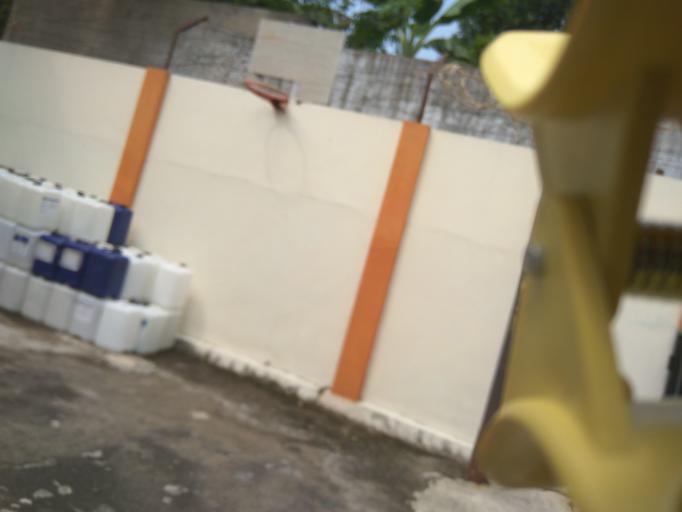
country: ID
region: Central Java
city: Semarang
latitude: -7.0437
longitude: 110.4178
